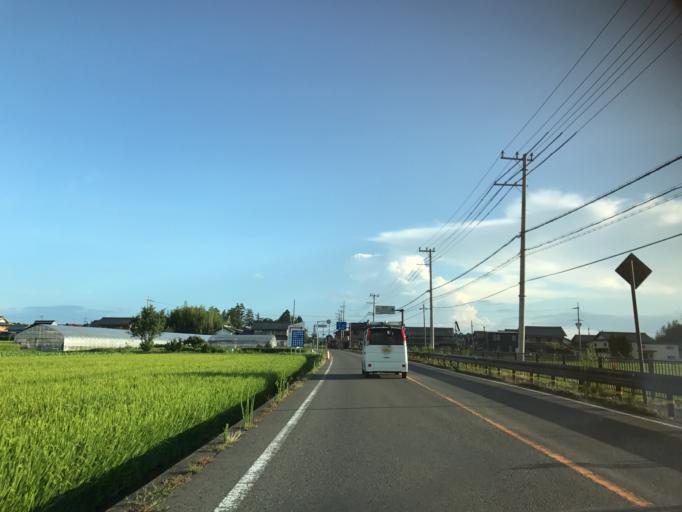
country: JP
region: Shiga Prefecture
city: Youkaichi
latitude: 35.1273
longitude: 136.2589
